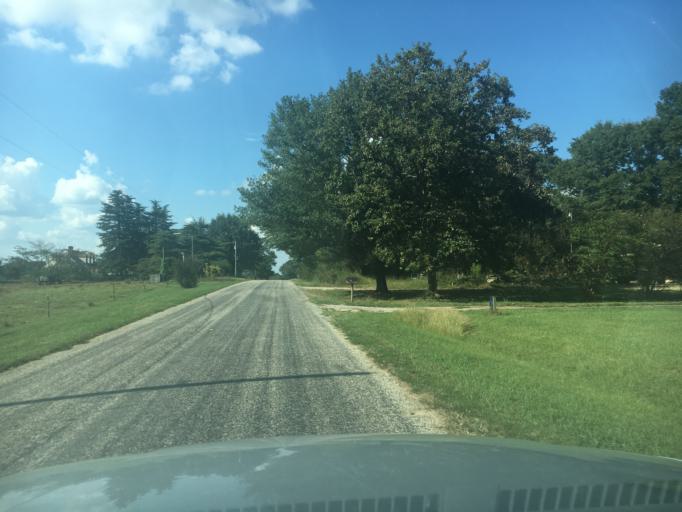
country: US
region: South Carolina
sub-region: Greenwood County
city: Ware Shoals
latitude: 34.4752
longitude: -82.2405
